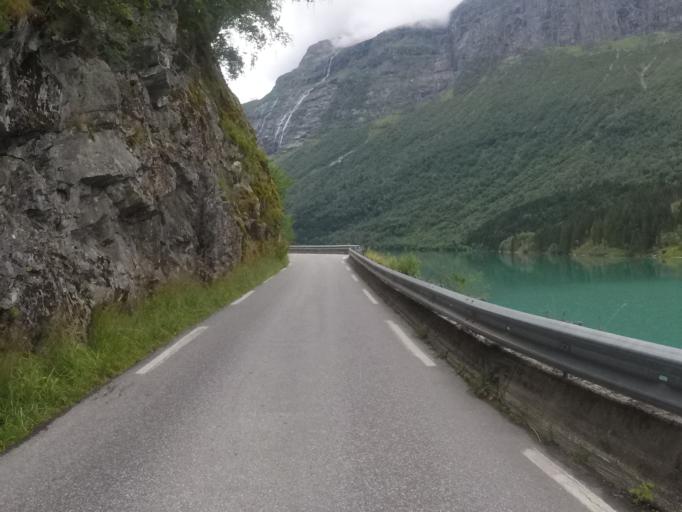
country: NO
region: Sogn og Fjordane
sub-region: Stryn
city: Stryn
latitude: 61.8560
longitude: 6.8956
